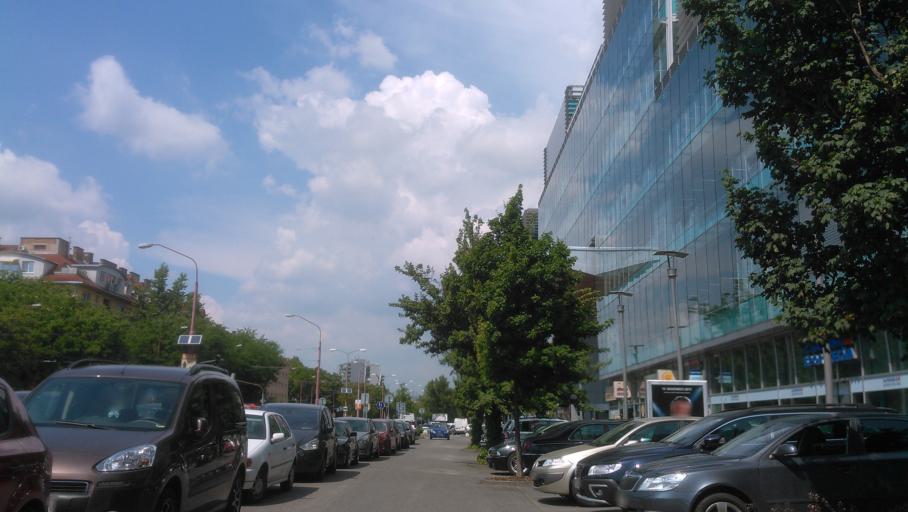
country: SK
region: Bratislavsky
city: Bratislava
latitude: 48.1484
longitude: 17.1252
